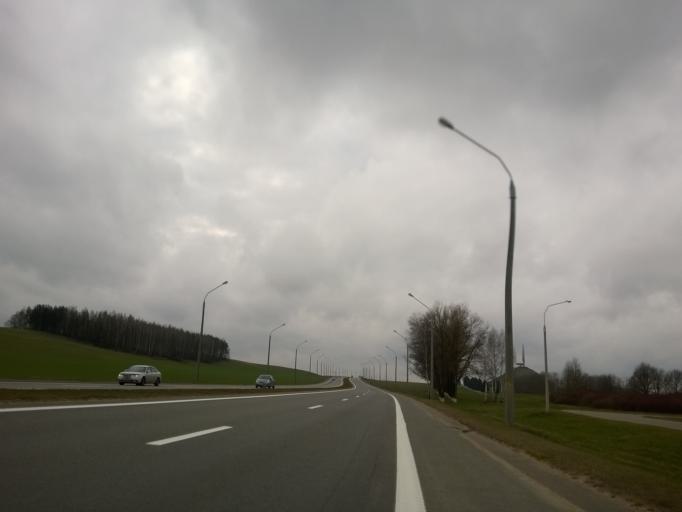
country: BY
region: Minsk
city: Slabada
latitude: 54.0205
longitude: 27.9125
